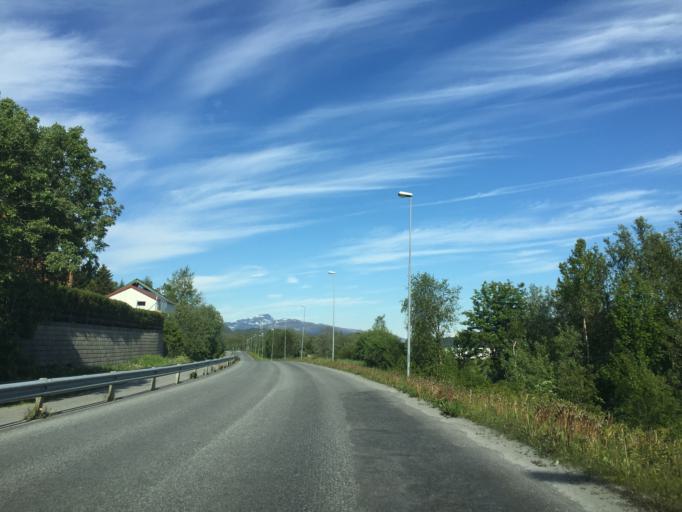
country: NO
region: Nordland
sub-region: Bodo
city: Lopsmarka
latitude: 67.2878
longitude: 14.5770
